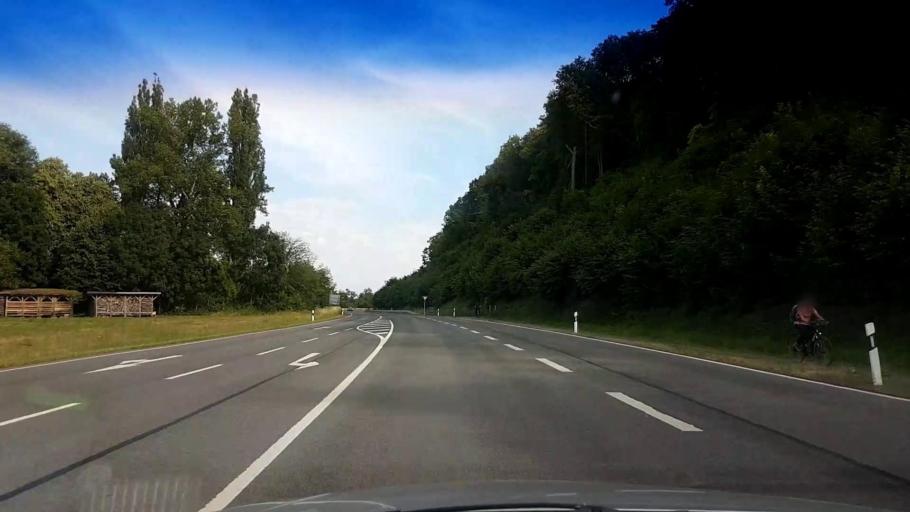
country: DE
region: Bavaria
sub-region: Regierungsbezirk Unterfranken
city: Stettfeld
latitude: 49.9656
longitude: 10.7033
